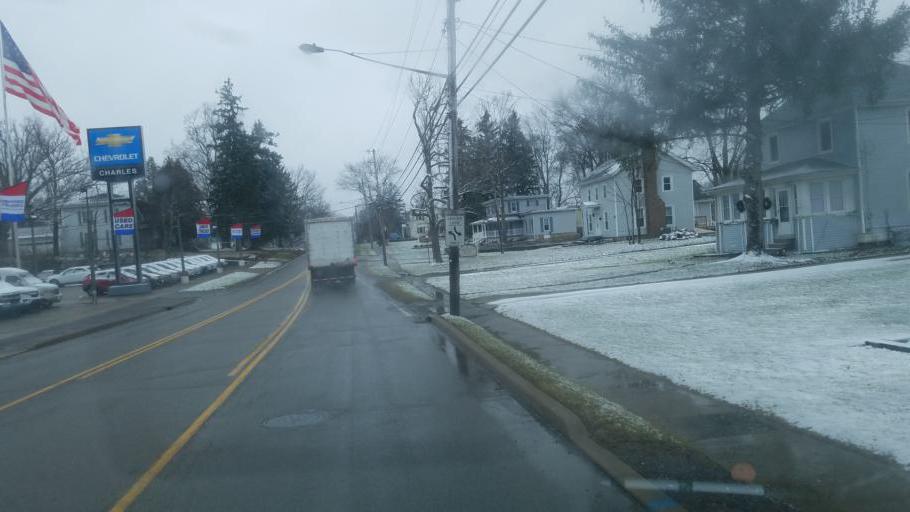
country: US
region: Ohio
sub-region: Portage County
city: Garrettsville
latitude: 41.2872
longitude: -81.0986
